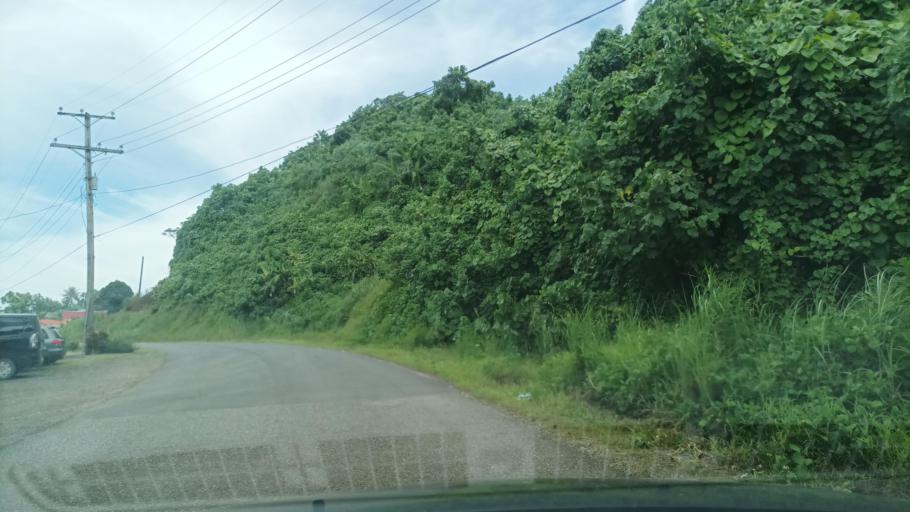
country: FM
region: Kosrae
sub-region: Lelu Municipality
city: Tofol
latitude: 5.3249
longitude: 163.0090
